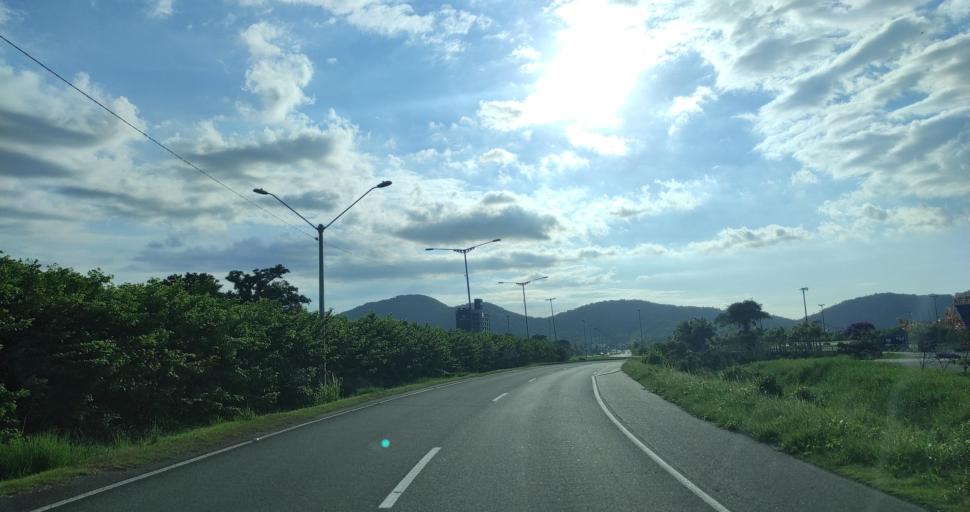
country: BR
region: Santa Catarina
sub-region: Penha
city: Penha
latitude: -26.7977
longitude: -48.6229
